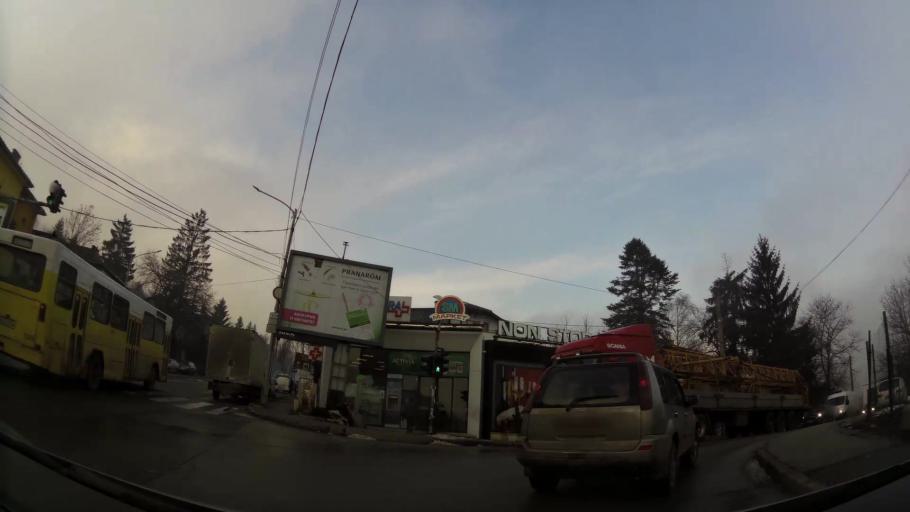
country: BG
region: Sofia-Capital
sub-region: Stolichna Obshtina
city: Sofia
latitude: 42.6498
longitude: 23.2610
